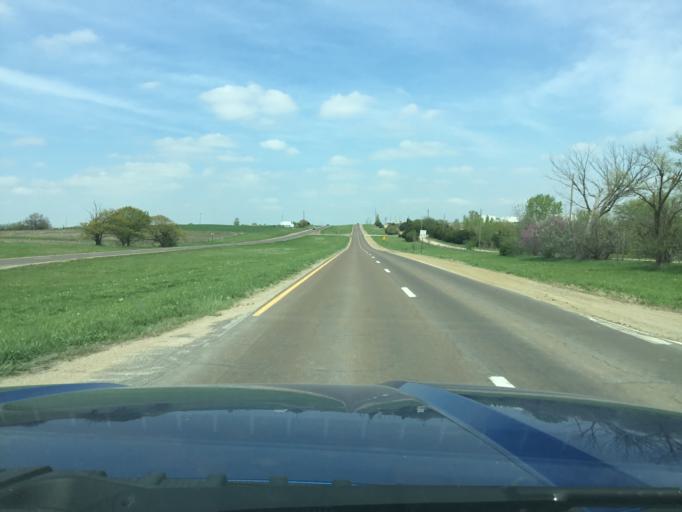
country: US
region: Kansas
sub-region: Osage County
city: Carbondale
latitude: 38.9136
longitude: -95.6874
